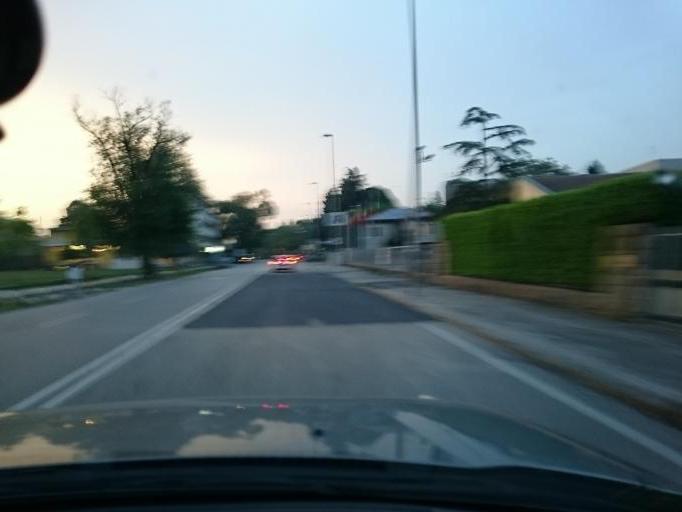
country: IT
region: Veneto
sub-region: Provincia di Padova
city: Padova
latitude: 45.4123
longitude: 11.9026
